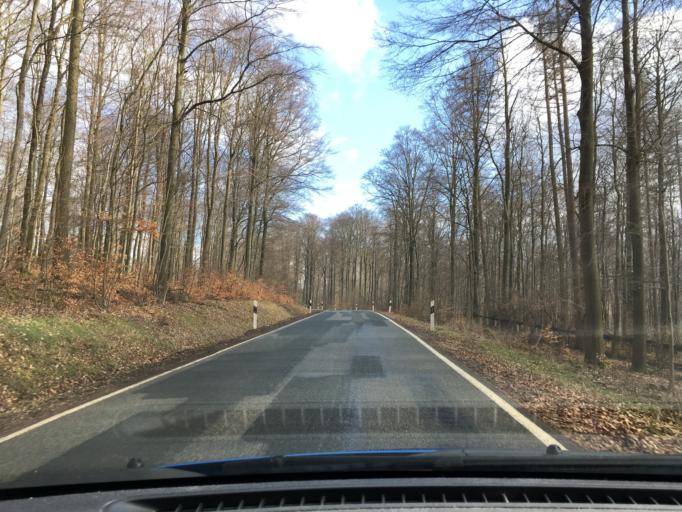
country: DE
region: Lower Saxony
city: Buhren
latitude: 51.4992
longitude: 9.6436
